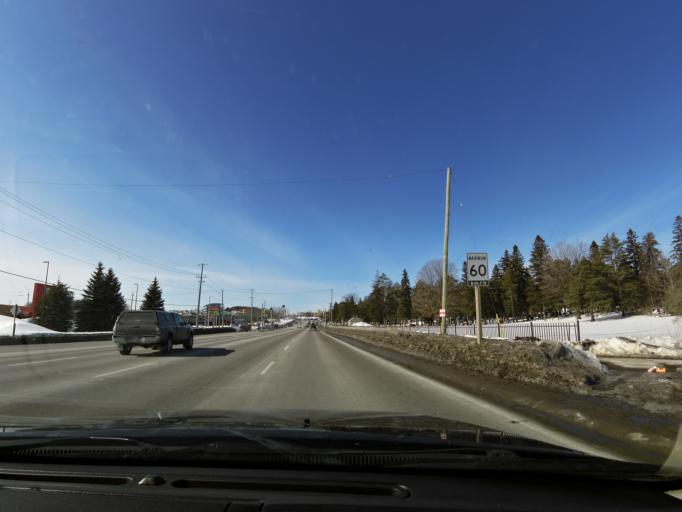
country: CA
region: Ontario
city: Orillia
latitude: 44.6112
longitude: -79.4490
